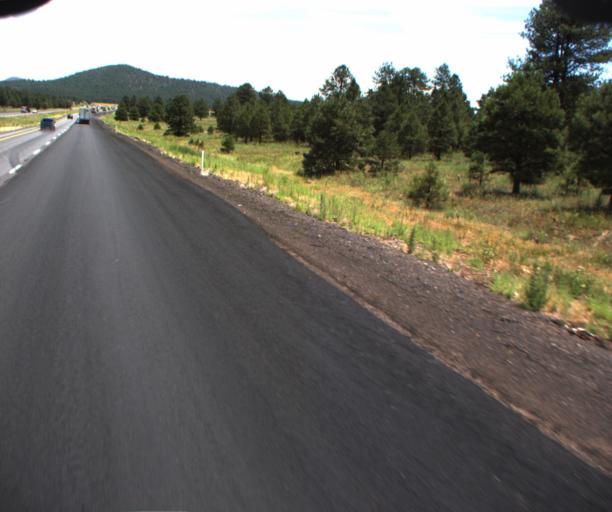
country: US
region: Arizona
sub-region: Coconino County
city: Williams
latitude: 35.2583
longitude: -112.1001
